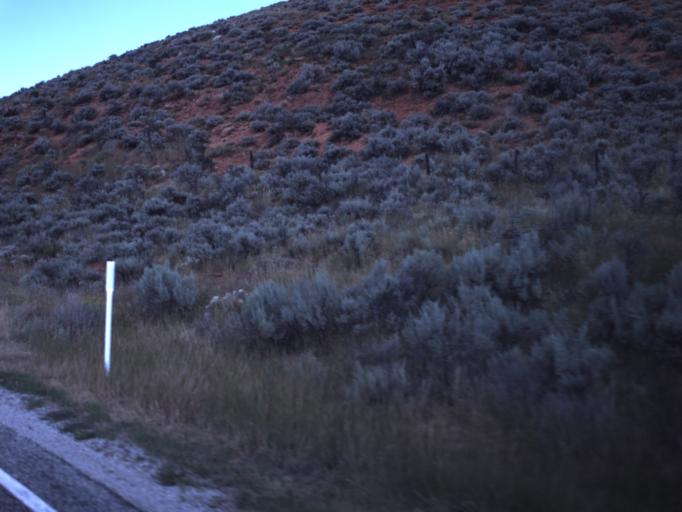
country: US
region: Utah
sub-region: Rich County
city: Randolph
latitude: 41.7887
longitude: -111.2117
